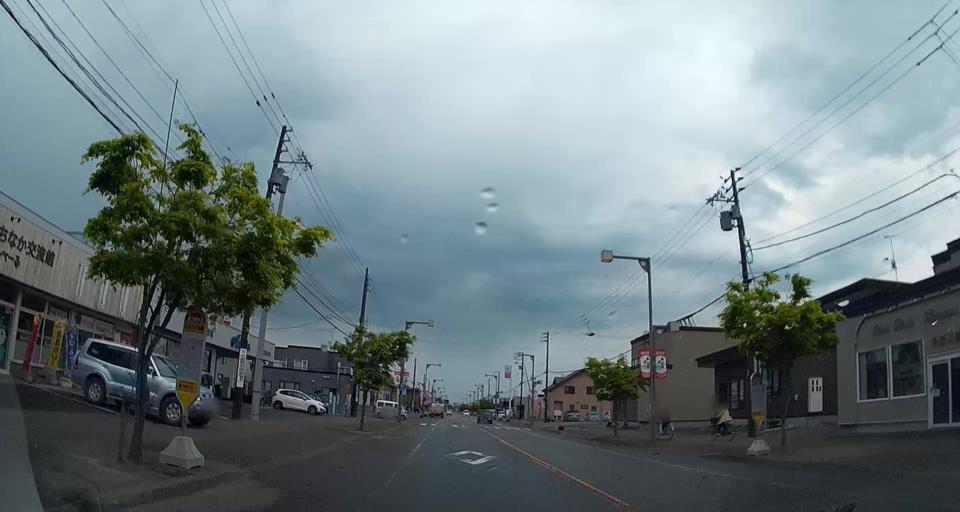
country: JP
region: Hokkaido
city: Chitose
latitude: 42.7253
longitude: 141.8784
